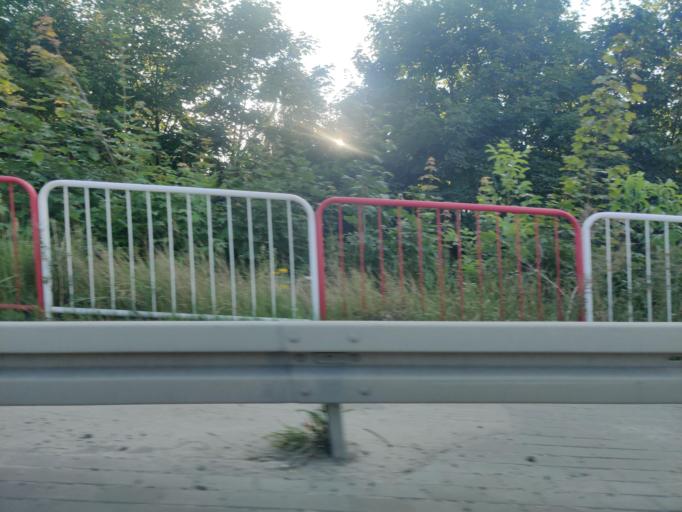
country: PL
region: Greater Poland Voivodeship
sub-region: Konin
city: Konin
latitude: 52.2311
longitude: 18.2453
